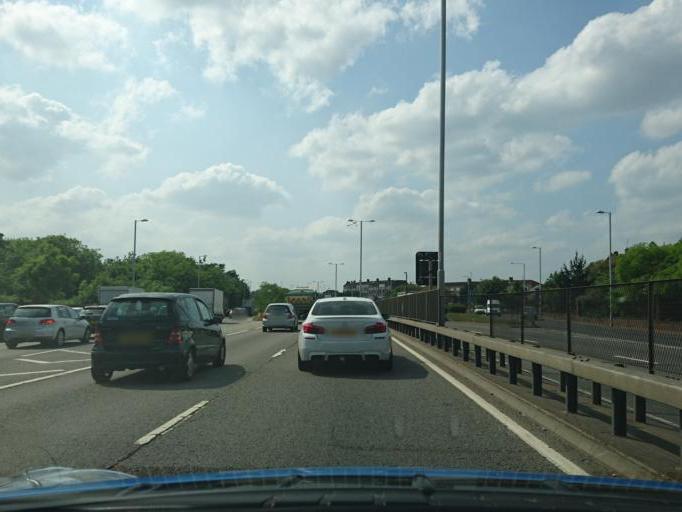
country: GB
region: England
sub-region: Greater London
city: Enfield
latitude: 51.6154
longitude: -0.0814
